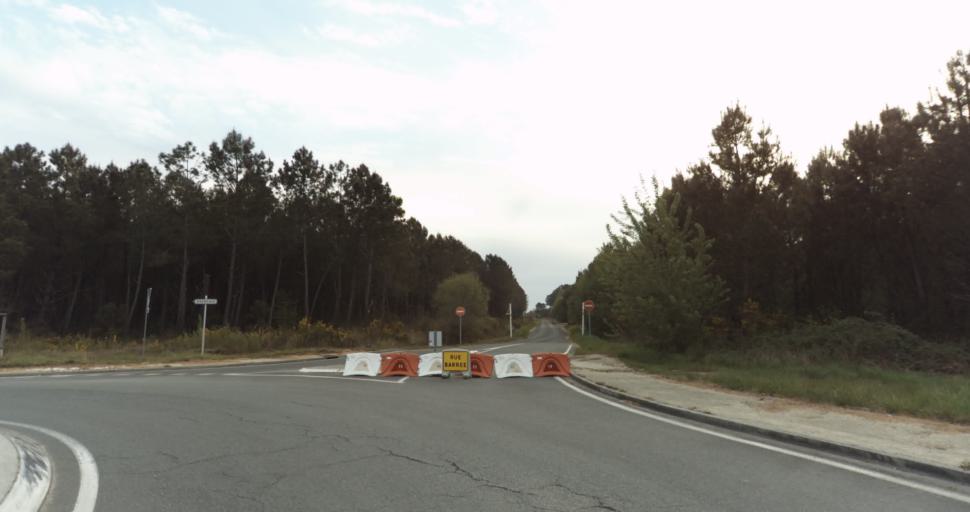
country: FR
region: Aquitaine
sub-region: Departement de la Gironde
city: Martignas-sur-Jalle
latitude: 44.7837
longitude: -0.7743
